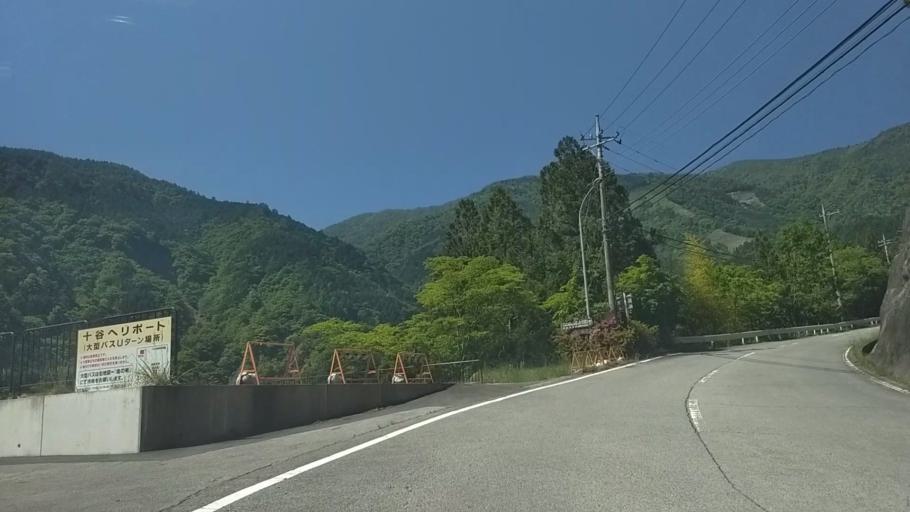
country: JP
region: Yamanashi
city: Ryuo
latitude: 35.5068
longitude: 138.4008
